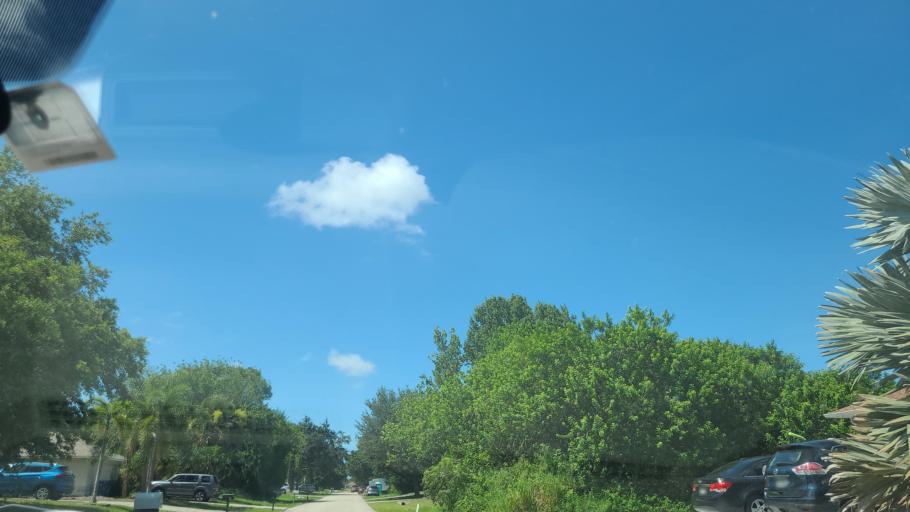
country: US
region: Florida
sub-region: Indian River County
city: Sebastian
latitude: 27.7683
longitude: -80.4957
